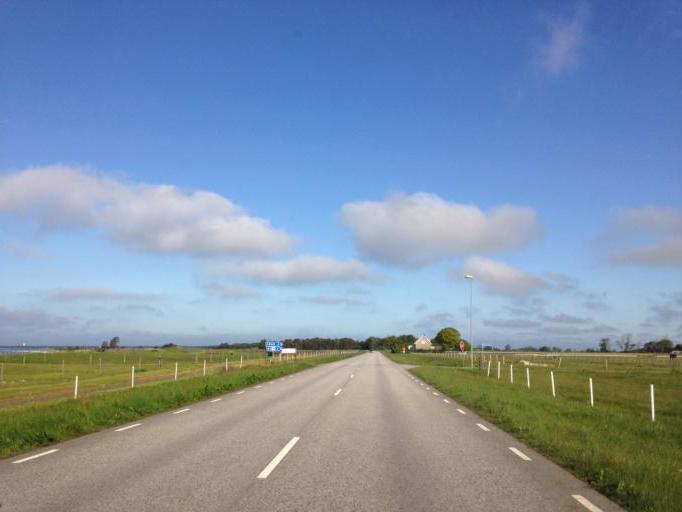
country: SE
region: Skane
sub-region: Trelleborgs Kommun
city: Skare
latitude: 55.3902
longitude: 13.0097
